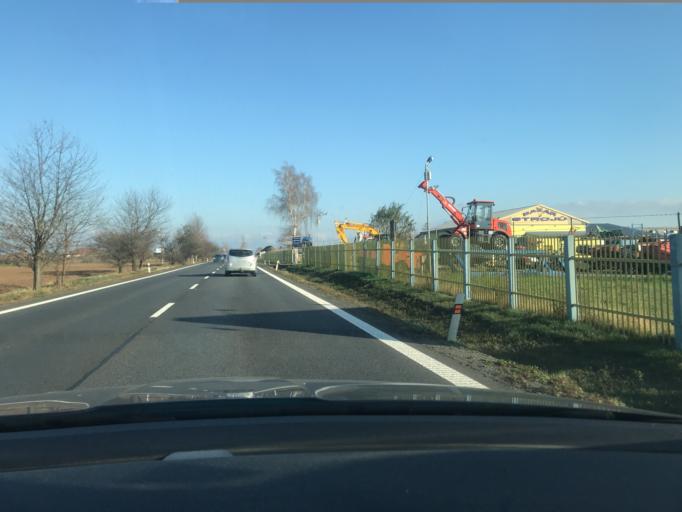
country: CZ
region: Kralovehradecky
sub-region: Okres Hradec Kralove
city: Smirice
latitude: 50.3008
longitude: 15.8484
